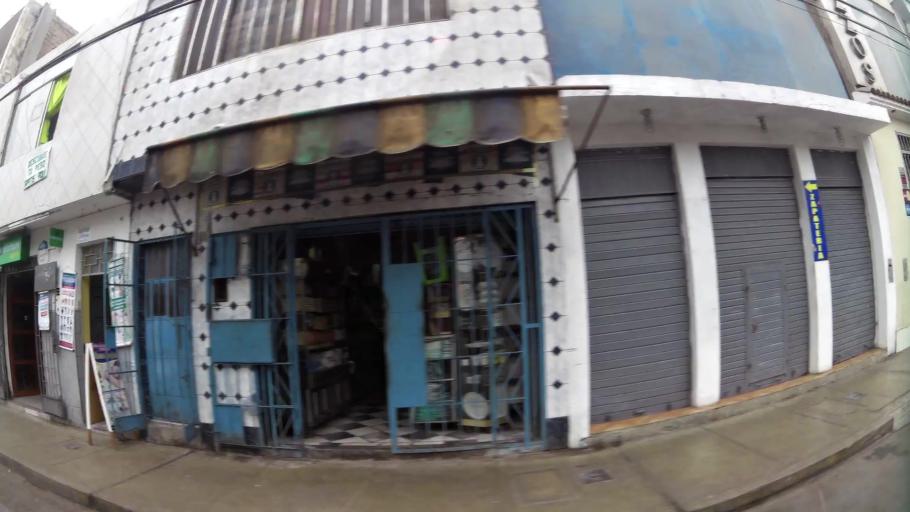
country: PE
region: Ica
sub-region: Provincia de Pisco
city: Pisco
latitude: -13.7121
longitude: -76.2048
